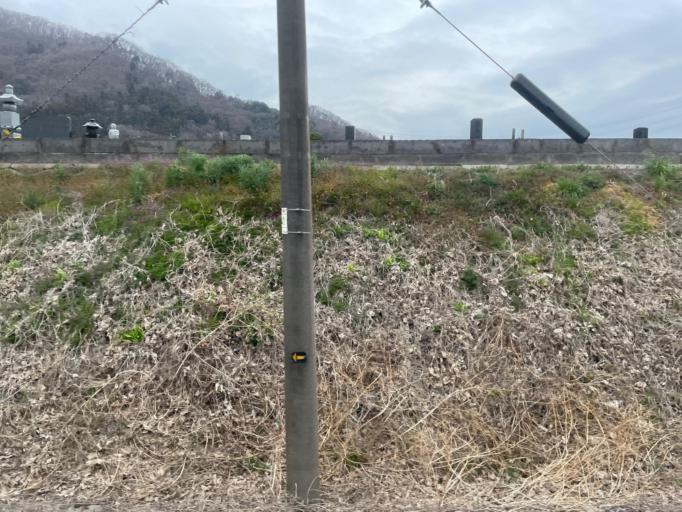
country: JP
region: Gunma
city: Numata
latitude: 36.5705
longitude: 139.0462
